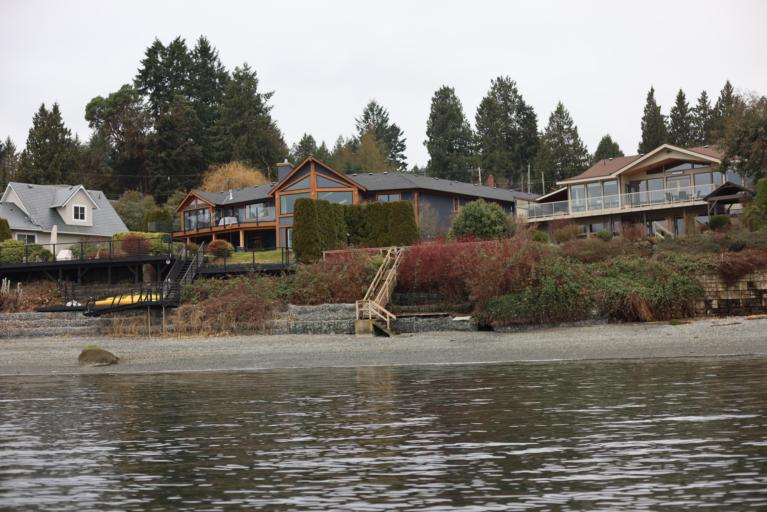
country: CA
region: British Columbia
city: North Saanich
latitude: 48.6432
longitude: -123.5436
